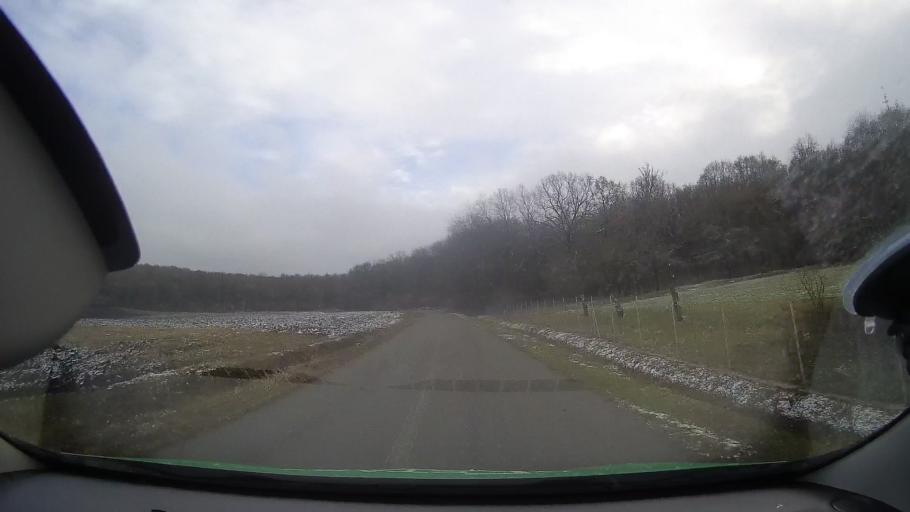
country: RO
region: Mures
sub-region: Comuna Chetani
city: Chetani
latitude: 46.4021
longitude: 24.0151
